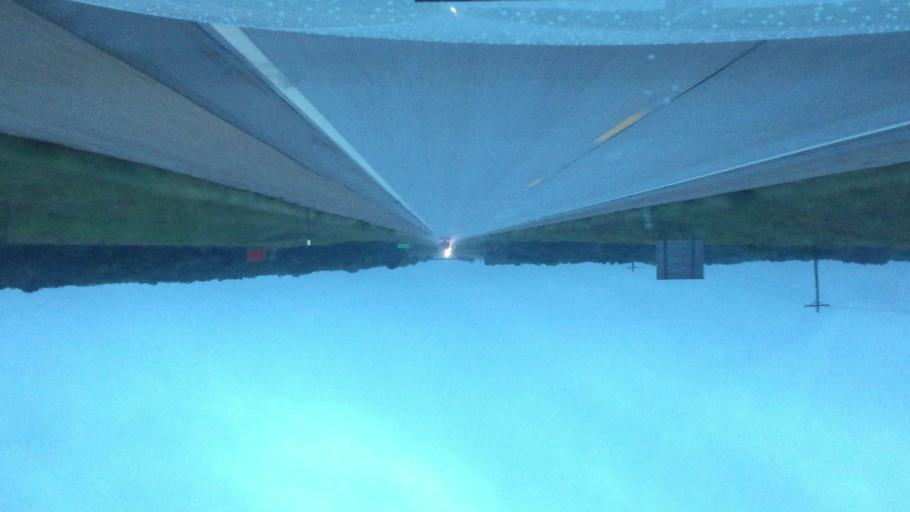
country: US
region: Kansas
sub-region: Allen County
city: Humboldt
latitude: 37.8045
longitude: -95.4114
